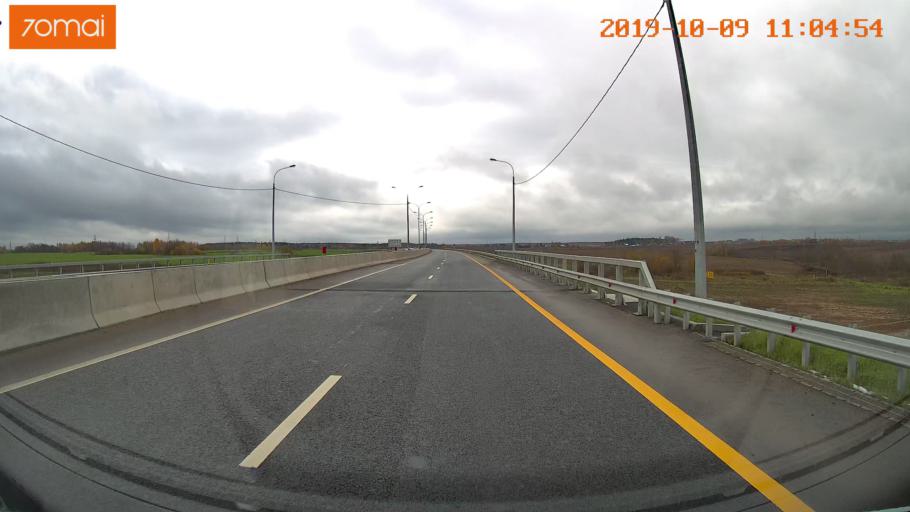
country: RU
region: Vologda
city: Molochnoye
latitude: 59.2066
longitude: 39.7622
